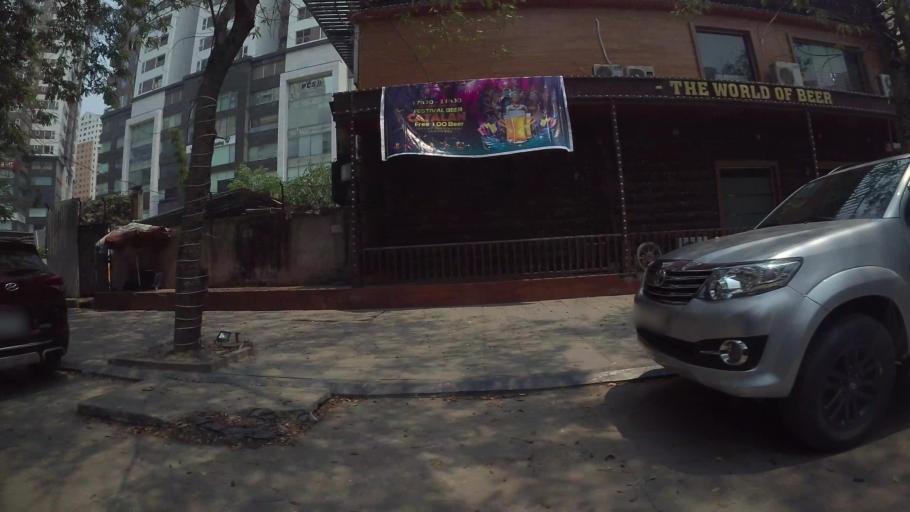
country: VN
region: Ha Noi
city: Thanh Xuan
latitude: 21.0073
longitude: 105.8004
